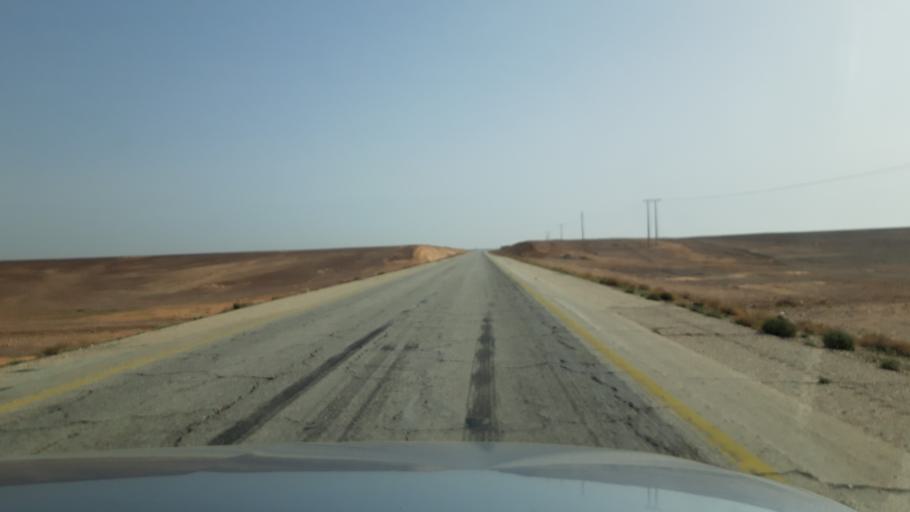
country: JO
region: Amman
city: Al Azraq ash Shamali
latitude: 31.8622
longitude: 36.7041
